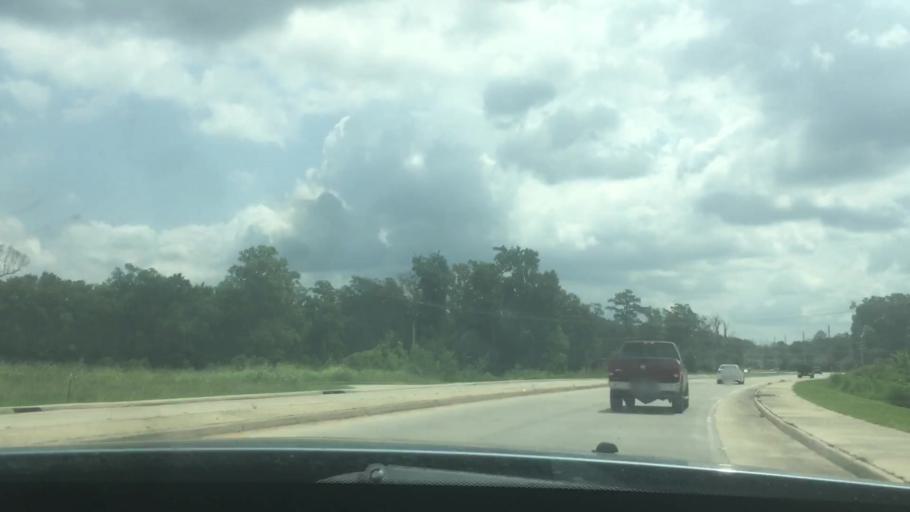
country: US
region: Louisiana
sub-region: East Baton Rouge Parish
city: Shenandoah
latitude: 30.4223
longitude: -91.0136
